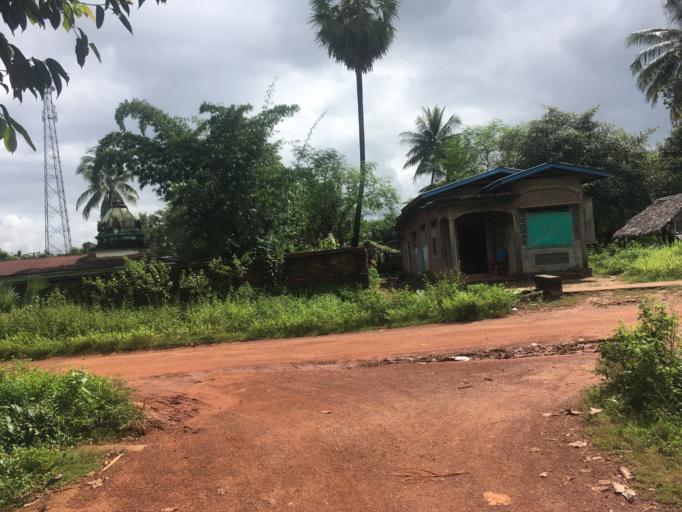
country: MM
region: Mon
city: Mawlamyine
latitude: 16.4650
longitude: 97.6908
